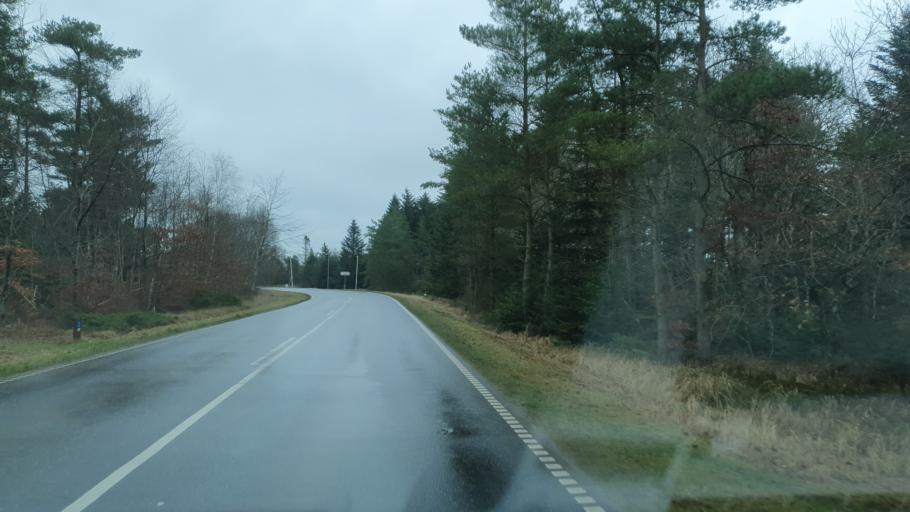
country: DK
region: North Denmark
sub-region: Jammerbugt Kommune
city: Fjerritslev
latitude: 57.1291
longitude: 9.1328
